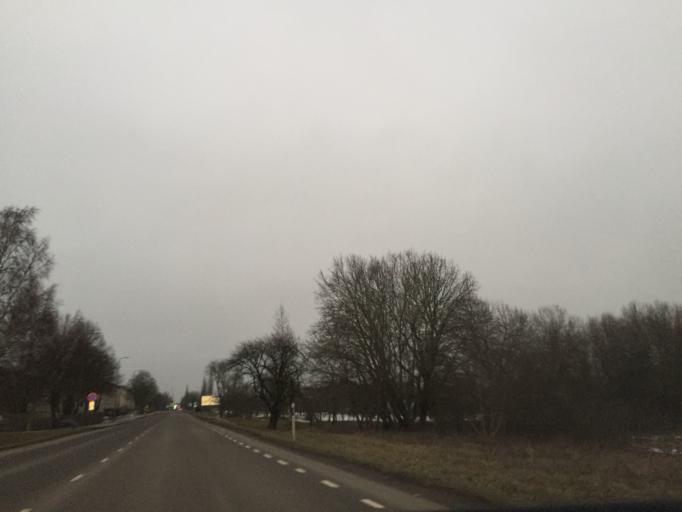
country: EE
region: Saare
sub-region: Kuressaare linn
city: Kuressaare
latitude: 58.2517
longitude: 22.5085
